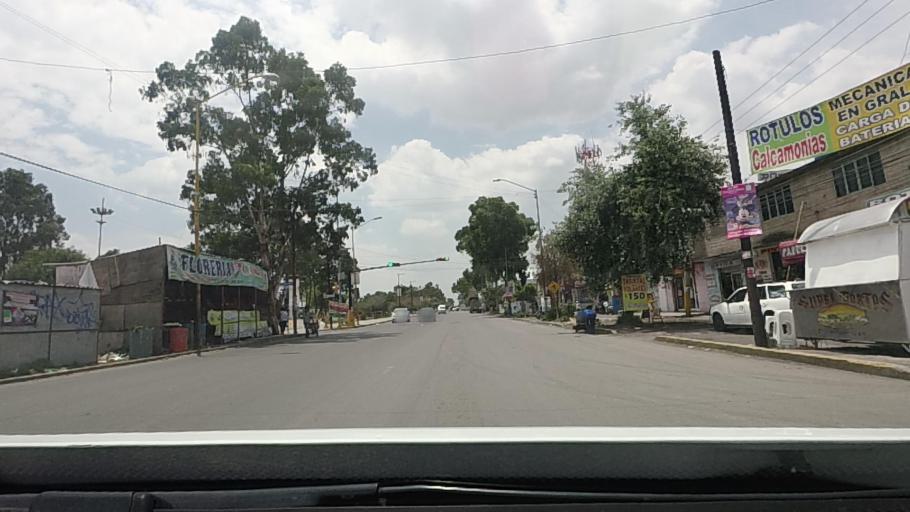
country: MX
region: Mexico
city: Chalco de Diaz Covarrubias
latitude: 19.2813
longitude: -98.9116
